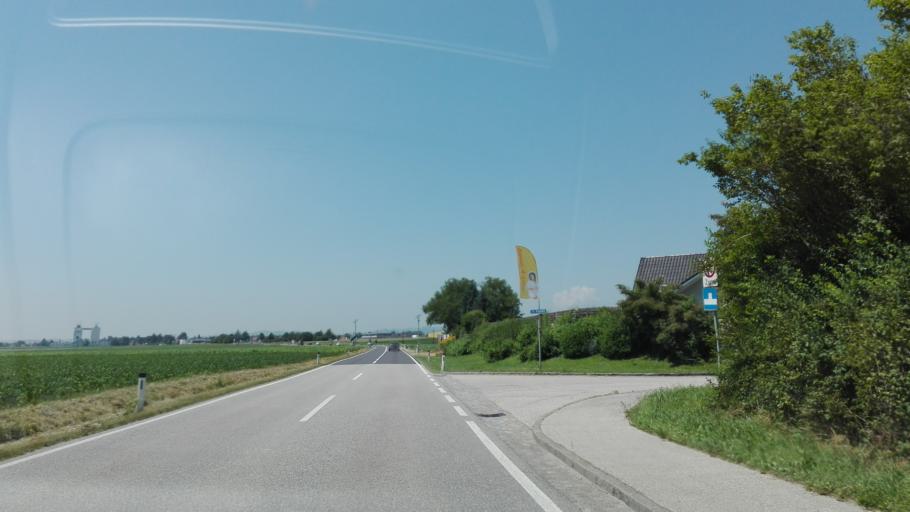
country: AT
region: Upper Austria
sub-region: Politischer Bezirk Urfahr-Umgebung
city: Goldworth
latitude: 48.2877
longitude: 14.1393
